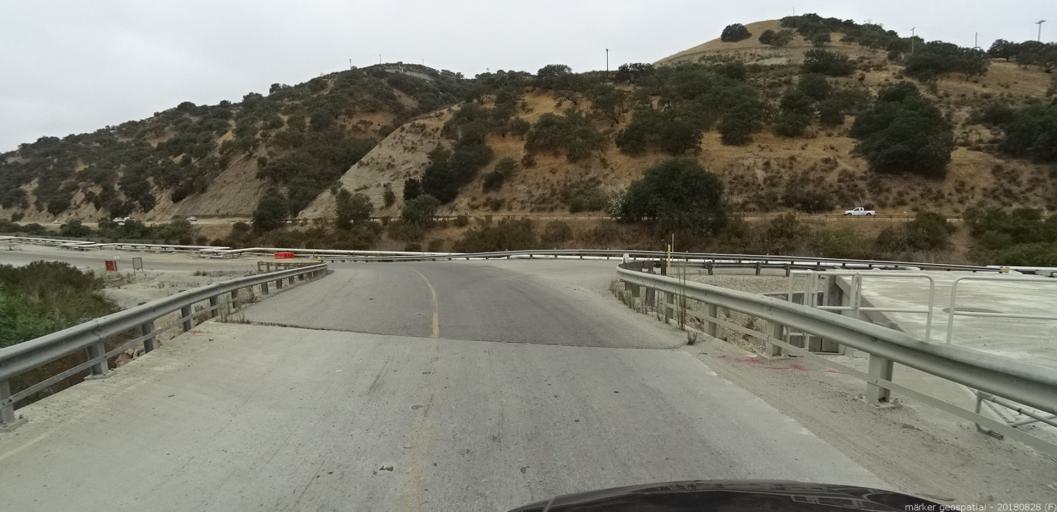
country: US
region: California
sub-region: San Luis Obispo County
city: Lake Nacimiento
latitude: 35.9606
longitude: -120.8830
